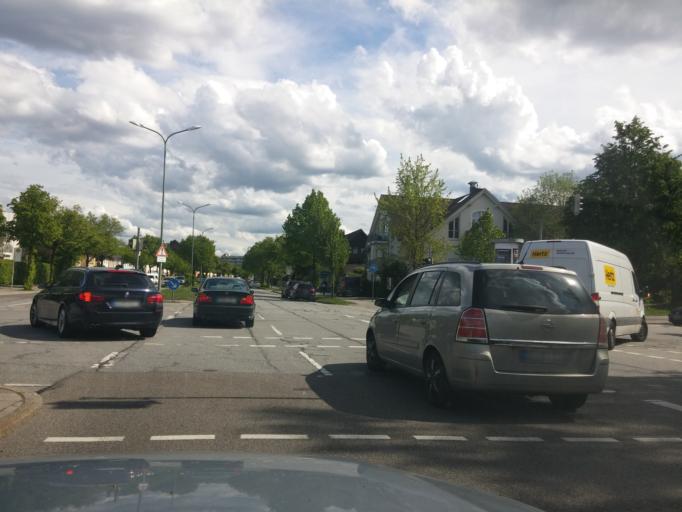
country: DE
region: Bavaria
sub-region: Upper Bavaria
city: Pullach im Isartal
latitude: 48.1069
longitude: 11.5222
